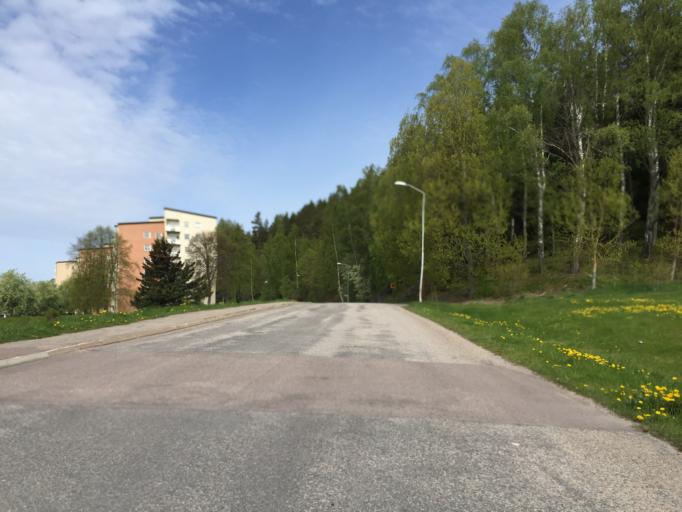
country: SE
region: Dalarna
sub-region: Ludvika Kommun
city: Ludvika
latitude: 60.1306
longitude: 15.1889
